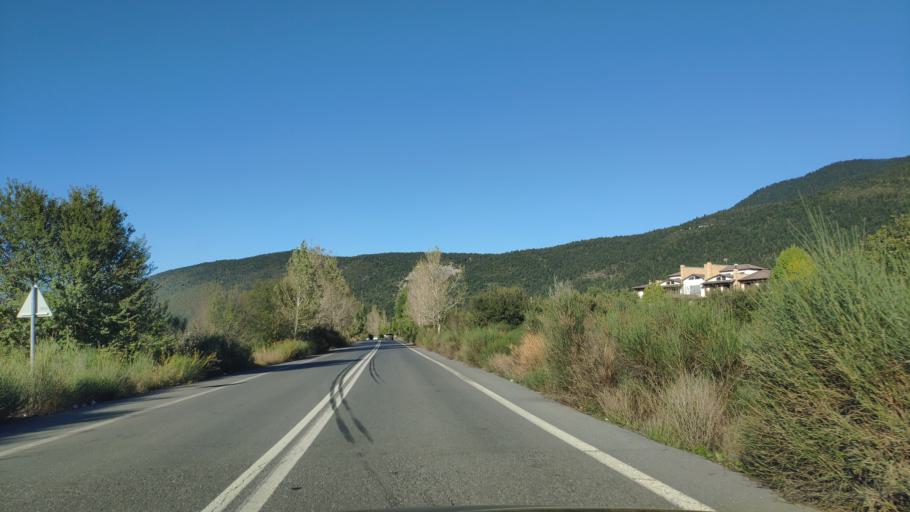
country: GR
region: Peloponnese
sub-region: Nomos Arkadias
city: Langadhia
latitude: 37.6864
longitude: 22.1927
